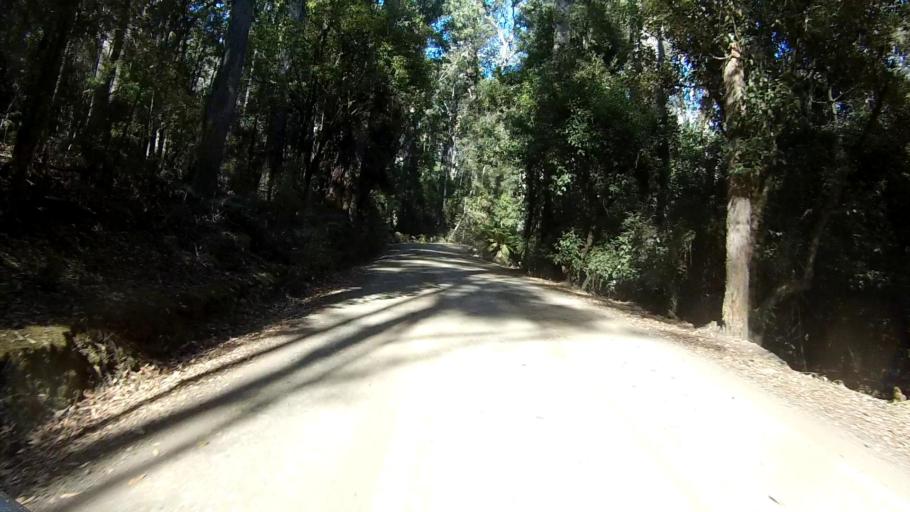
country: AU
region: Tasmania
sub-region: Derwent Valley
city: New Norfolk
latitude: -42.6820
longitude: 146.7121
